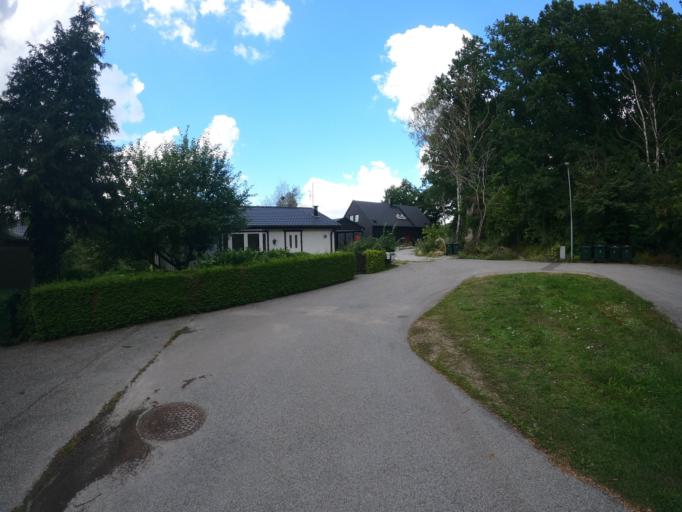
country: SE
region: Skane
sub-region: Lunds Kommun
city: Genarp
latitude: 55.6777
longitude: 13.3447
